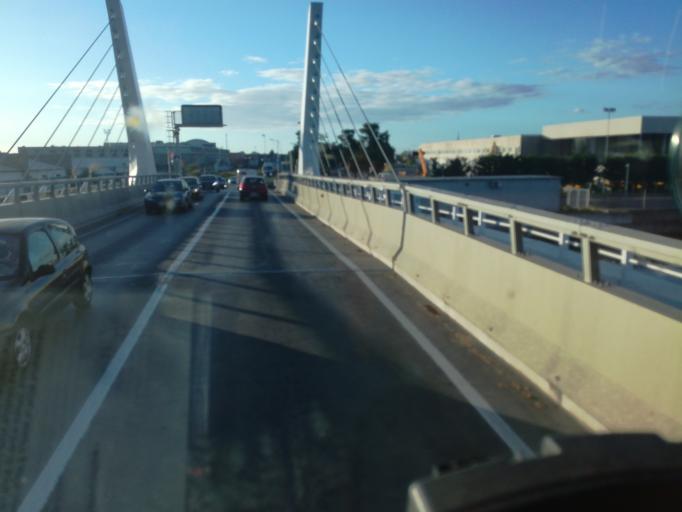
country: IT
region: Emilia-Romagna
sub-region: Provincia di Ravenna
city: Ravenna
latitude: 44.4291
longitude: 12.2254
